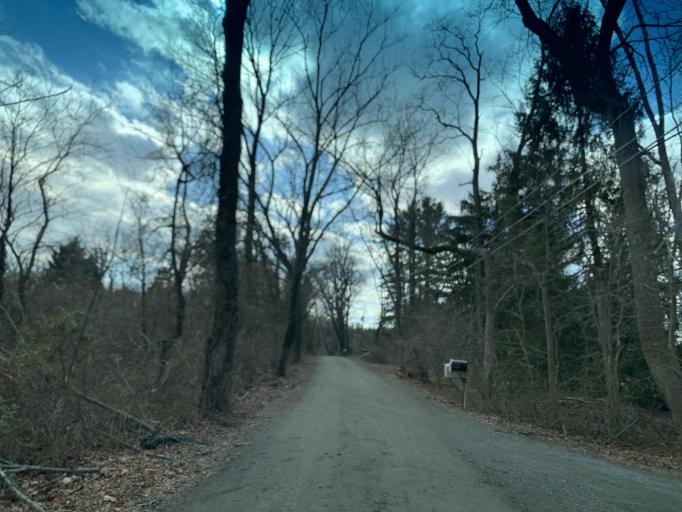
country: US
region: Maryland
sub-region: Harford County
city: Riverside
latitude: 39.5067
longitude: -76.2496
